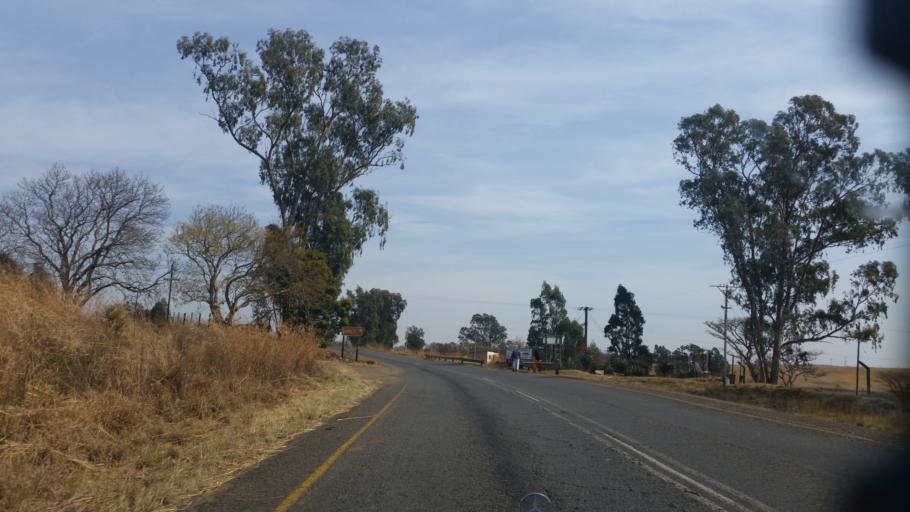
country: ZA
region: KwaZulu-Natal
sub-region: uThukela District Municipality
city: Estcourt
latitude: -29.0689
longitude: 29.9546
